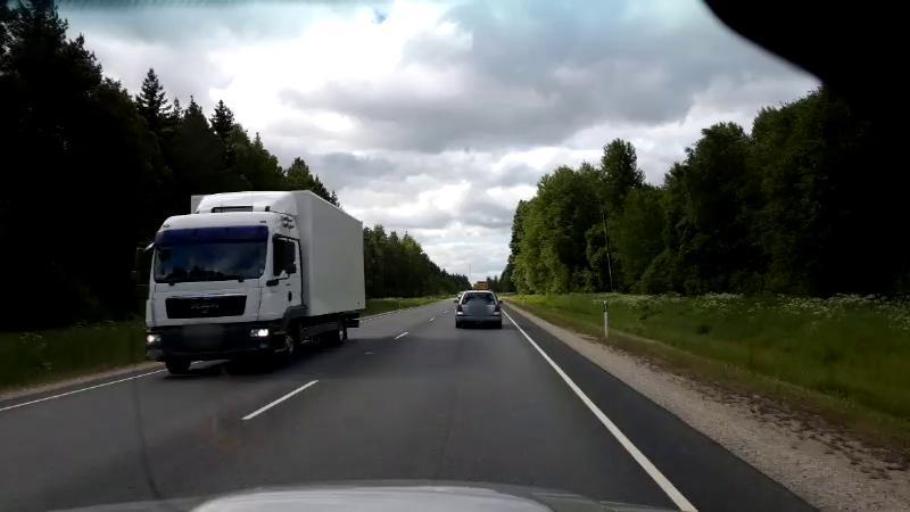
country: EE
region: Raplamaa
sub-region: Maerjamaa vald
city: Marjamaa
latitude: 58.7853
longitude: 24.4131
